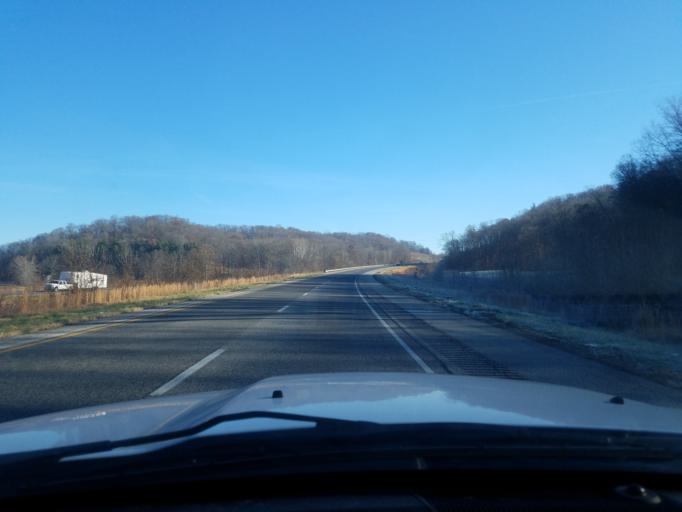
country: US
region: Indiana
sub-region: Dubois County
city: Ferdinand
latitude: 38.2097
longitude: -86.7756
